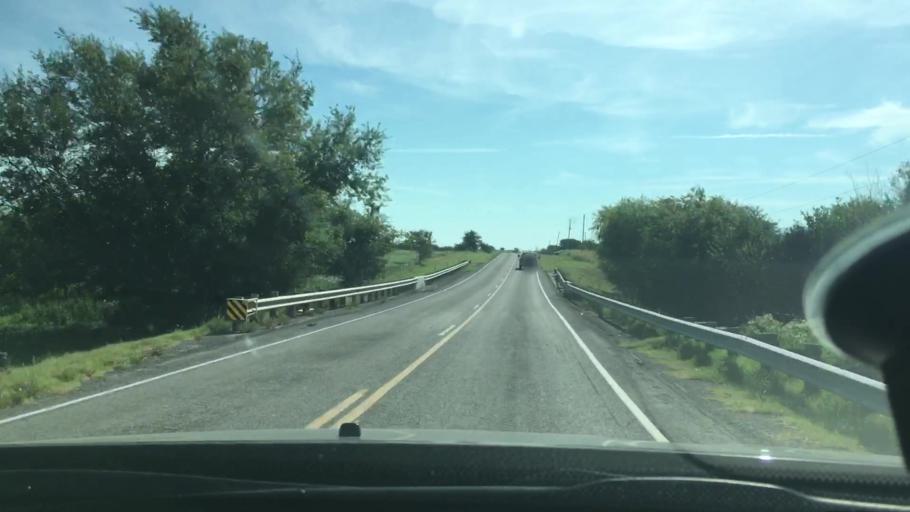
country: US
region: Oklahoma
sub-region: Carter County
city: Lone Grove
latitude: 34.3327
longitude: -97.2698
